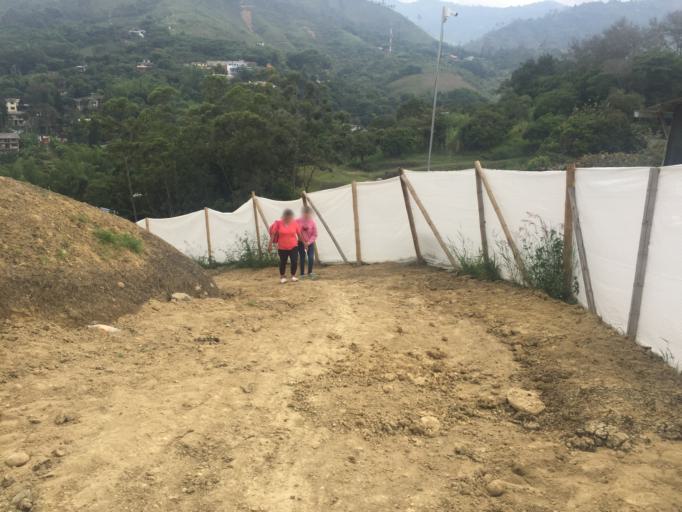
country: CO
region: Valle del Cauca
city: Cali
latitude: 3.4784
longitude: -76.5524
